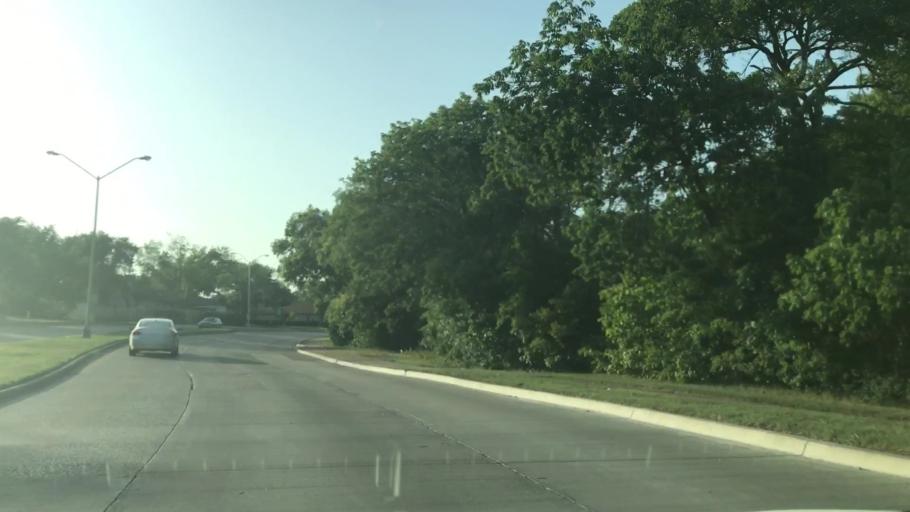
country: US
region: Texas
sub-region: Dallas County
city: Garland
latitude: 32.8593
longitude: -96.7009
